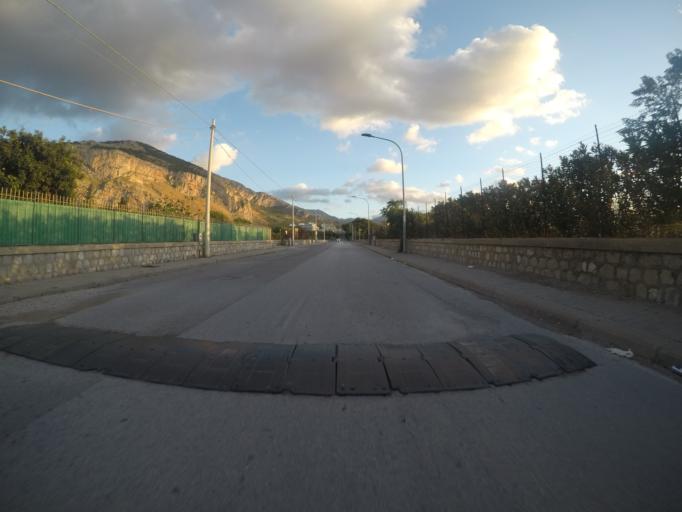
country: IT
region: Sicily
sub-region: Palermo
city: Isola delle Femmine
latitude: 38.1843
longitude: 13.2380
